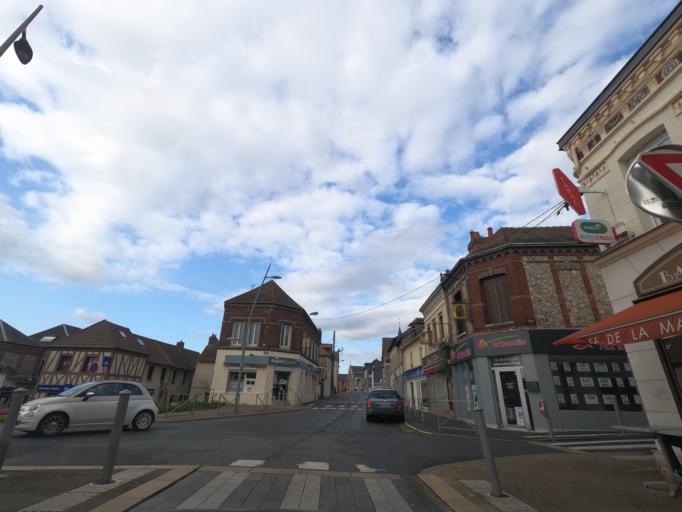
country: FR
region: Haute-Normandie
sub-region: Departement de la Seine-Maritime
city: Grand-Couronne
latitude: 49.3581
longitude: 1.0089
